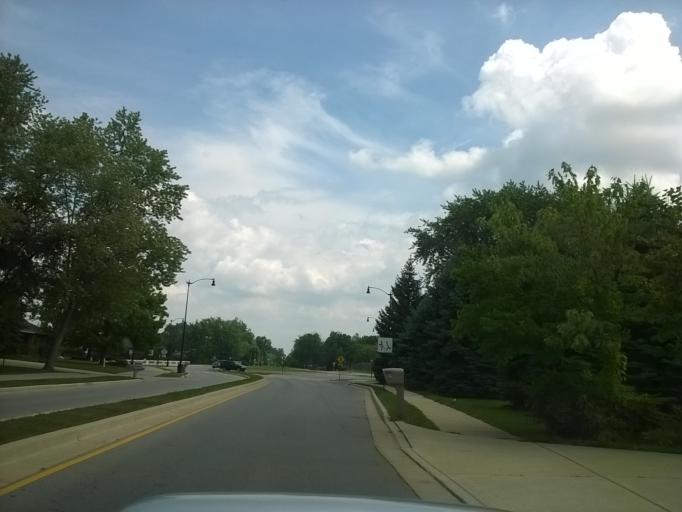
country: US
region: Indiana
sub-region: Hamilton County
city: Carmel
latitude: 39.9784
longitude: -86.1146
